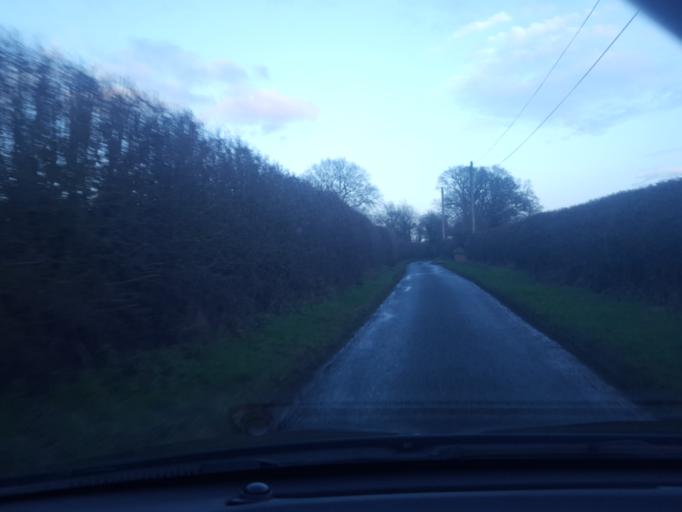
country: GB
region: England
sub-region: Shropshire
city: Albrighton
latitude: 52.6353
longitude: -2.2569
